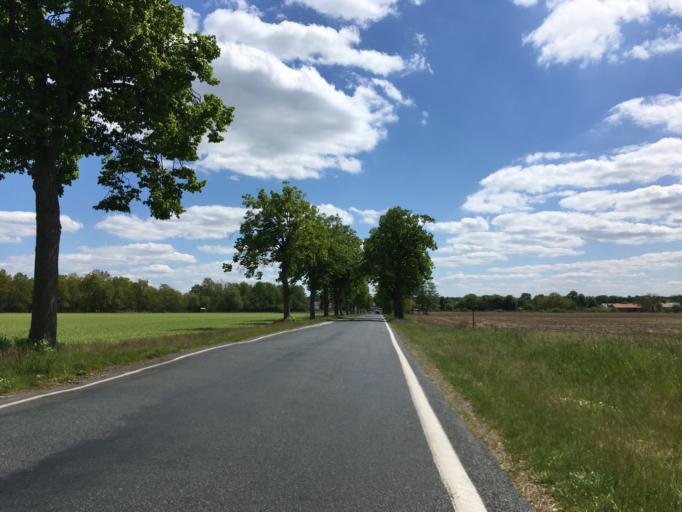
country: DE
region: Brandenburg
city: Wandlitz
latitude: 52.7809
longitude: 13.4309
